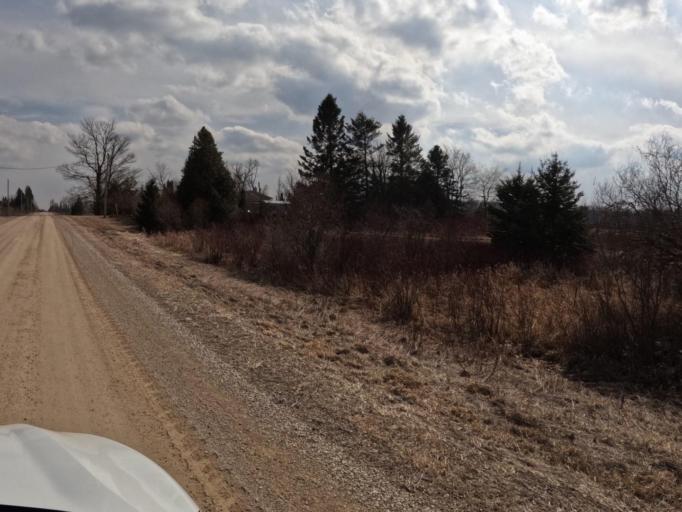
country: CA
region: Ontario
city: Shelburne
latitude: 43.9429
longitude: -80.3113
